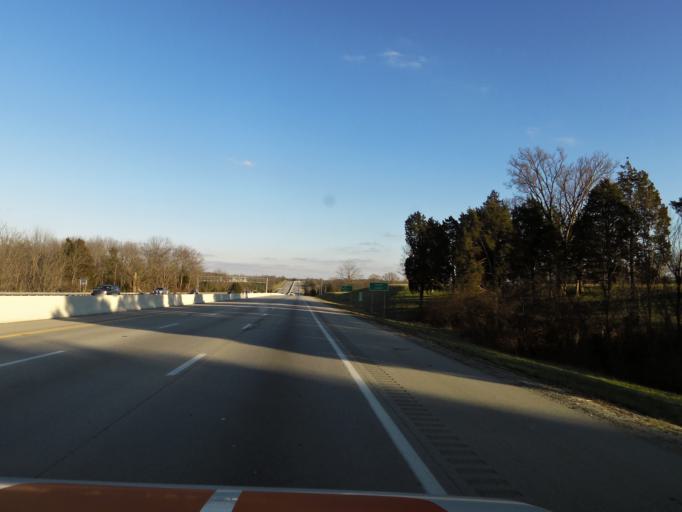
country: US
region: Kentucky
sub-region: Shelby County
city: Simpsonville
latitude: 38.2176
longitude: -85.4132
